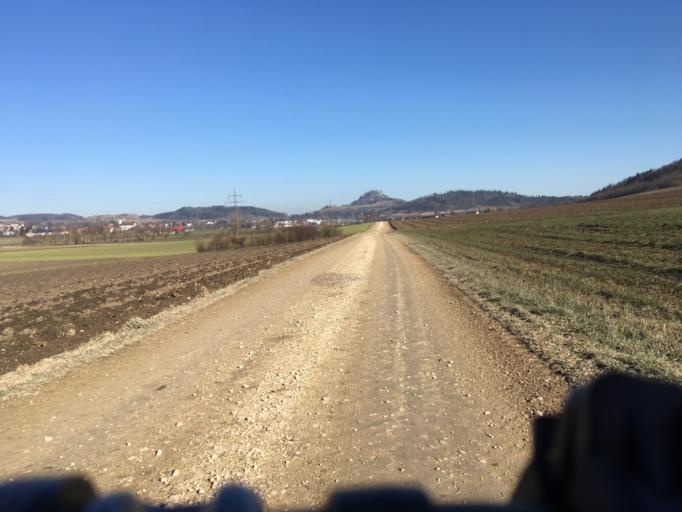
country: DE
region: Baden-Wuerttemberg
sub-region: Freiburg Region
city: Hilzingen
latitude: 47.7547
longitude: 8.7635
